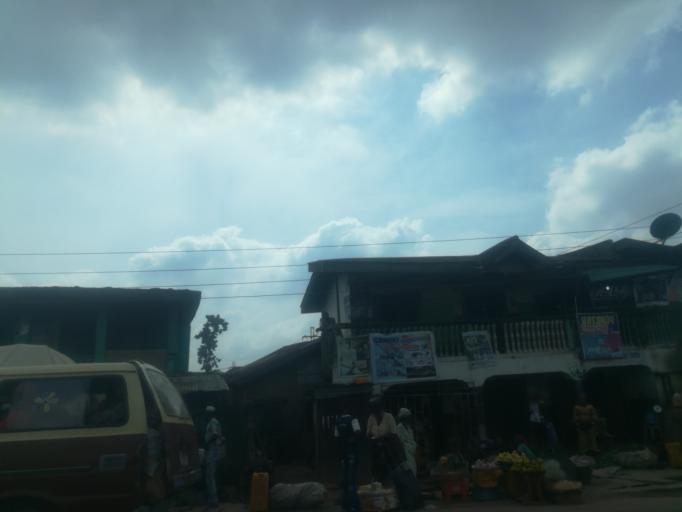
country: NG
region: Oyo
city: Ibadan
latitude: 7.3883
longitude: 3.9073
